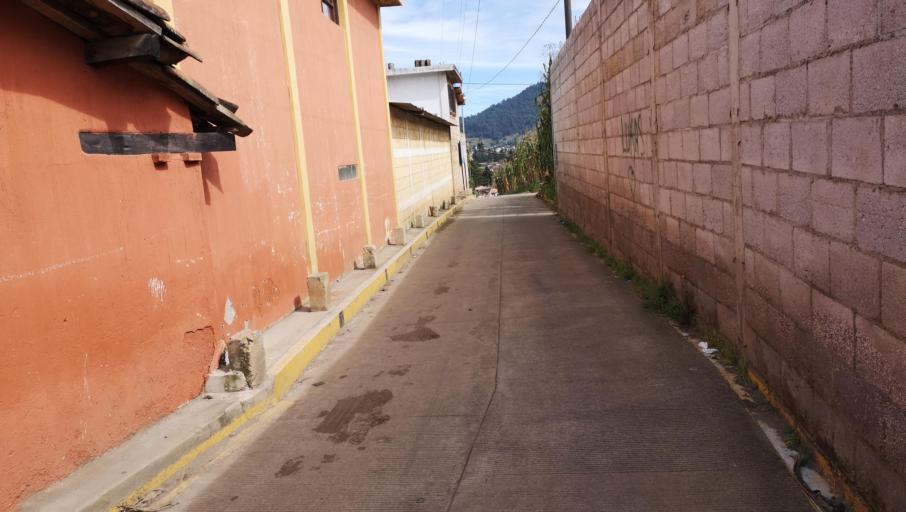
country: GT
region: Quetzaltenango
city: Cantel
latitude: 14.8185
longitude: -91.4413
